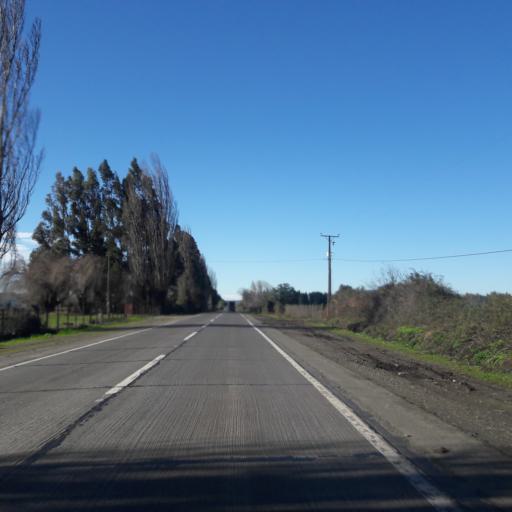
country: CL
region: Araucania
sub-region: Provincia de Malleco
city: Angol
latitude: -37.7705
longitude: -72.5524
